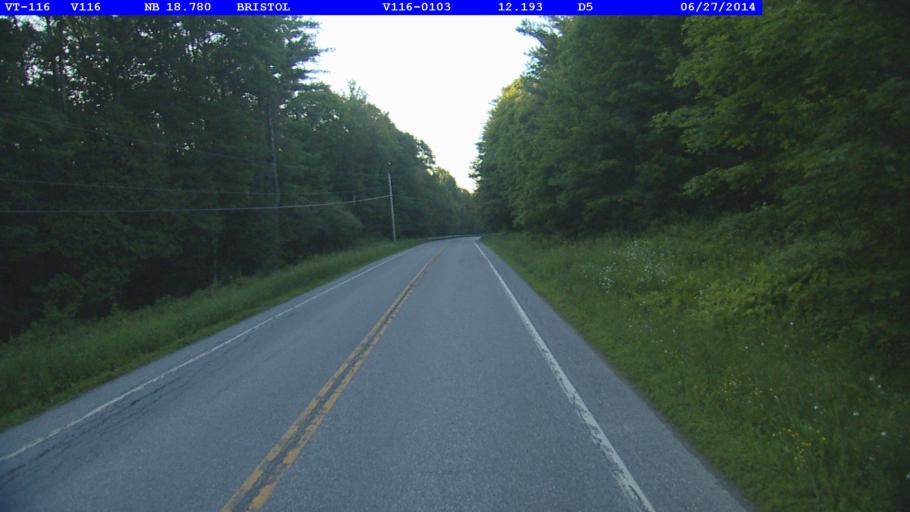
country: US
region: Vermont
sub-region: Addison County
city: Bristol
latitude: 44.1847
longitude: -73.0572
